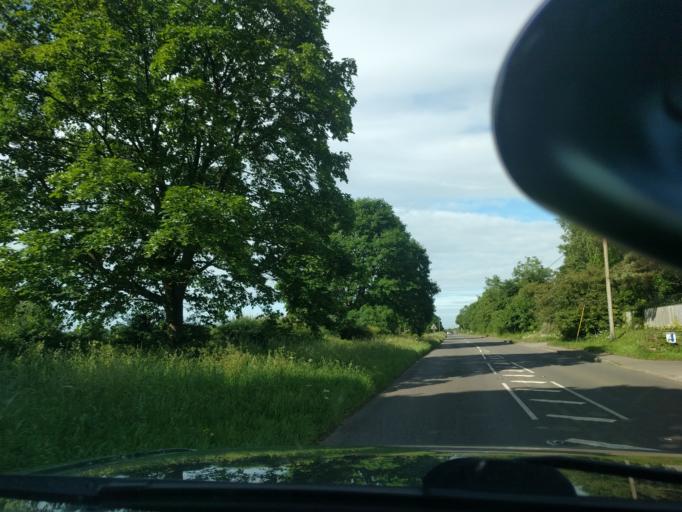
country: GB
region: England
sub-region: Wiltshire
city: Lyneham
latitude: 51.5224
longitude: -1.9562
